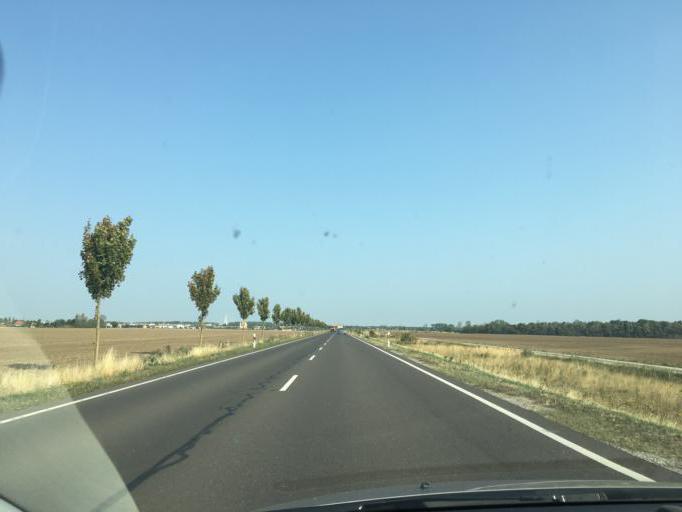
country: DE
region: Saxony-Anhalt
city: Schonebeck
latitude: 51.9983
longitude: 11.7743
